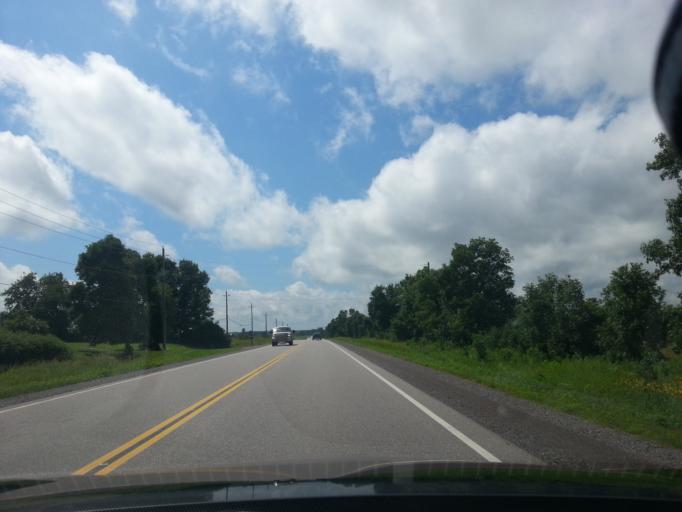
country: CA
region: Ontario
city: Renfrew
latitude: 45.5219
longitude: -76.8692
